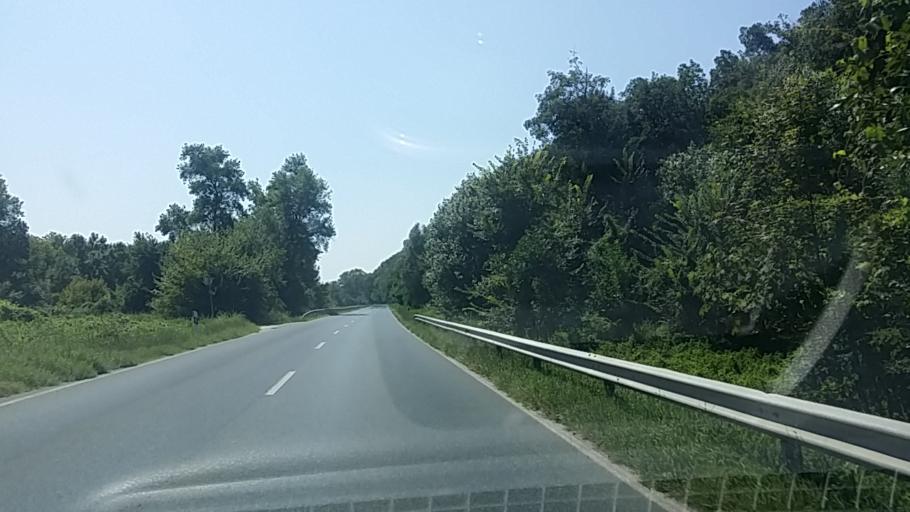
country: HU
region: Tolna
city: Paks
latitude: 46.6489
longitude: 18.8816
